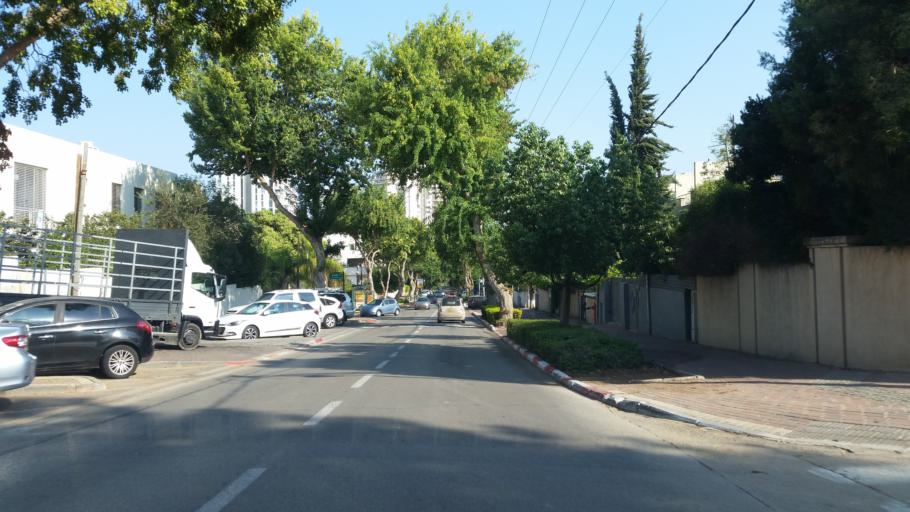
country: IL
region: Tel Aviv
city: Ramat HaSharon
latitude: 32.1462
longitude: 34.8450
